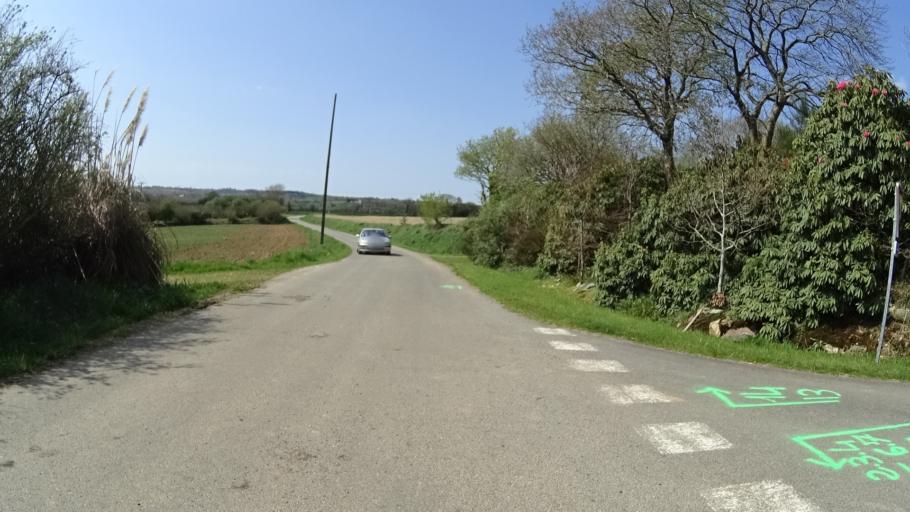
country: FR
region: Brittany
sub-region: Departement du Finistere
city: Sizun
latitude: 48.4402
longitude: -4.1113
